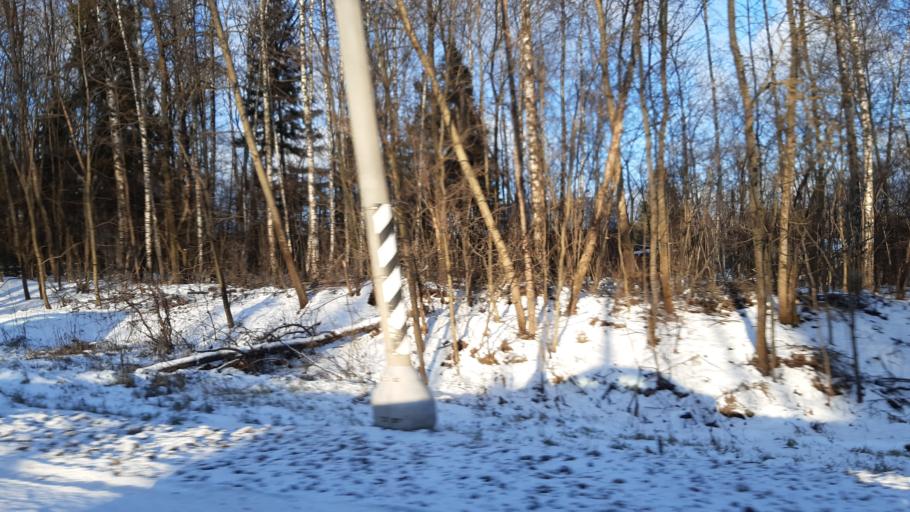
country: RU
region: Vladimir
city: Arsaki
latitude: 56.2980
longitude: 38.3585
